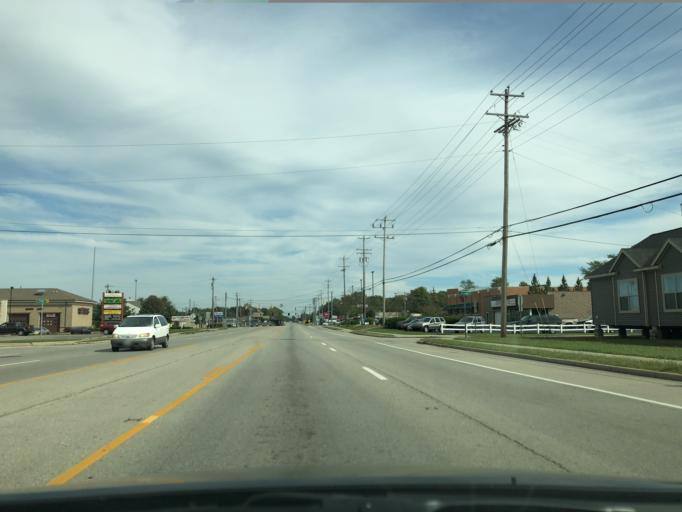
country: US
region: Ohio
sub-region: Clermont County
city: Mount Repose
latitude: 39.2010
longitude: -84.2240
